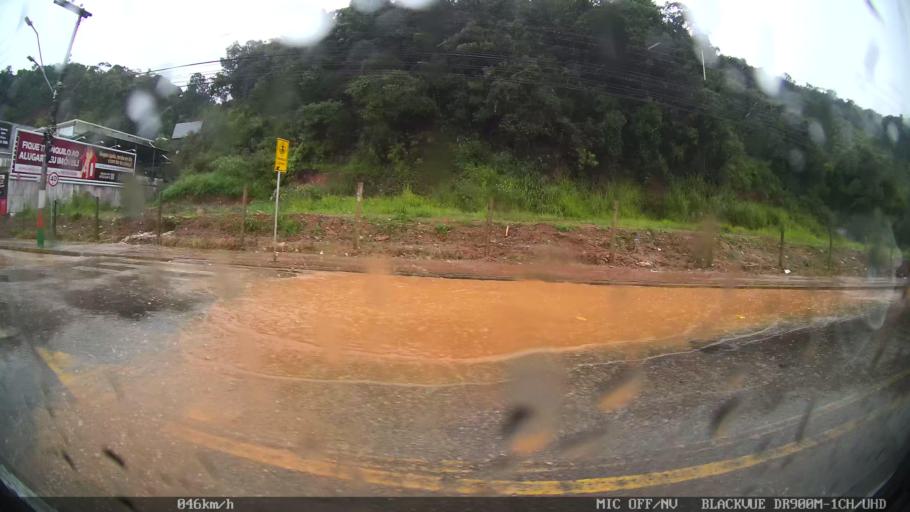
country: BR
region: Santa Catarina
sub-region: Balneario Camboriu
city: Balneario Camboriu
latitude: -27.0102
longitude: -48.6487
